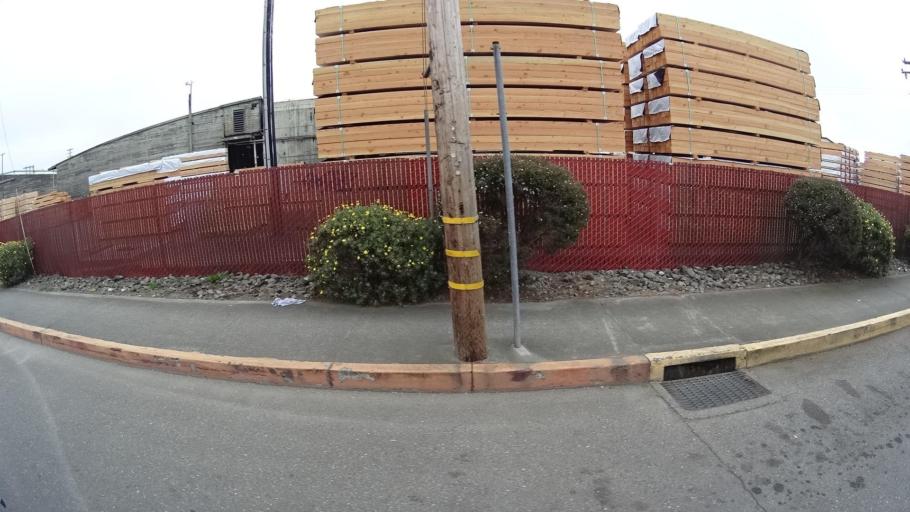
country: US
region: California
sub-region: Humboldt County
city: Eureka
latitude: 40.7953
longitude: -124.1833
